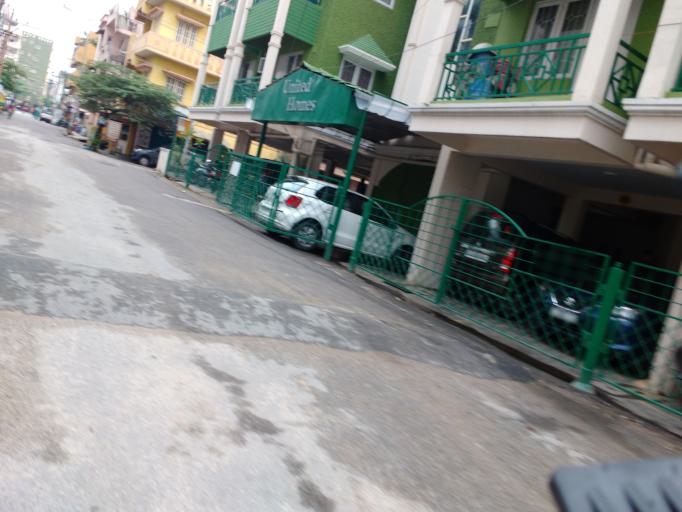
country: IN
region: Karnataka
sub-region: Bangalore Urban
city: Bangalore
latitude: 12.9917
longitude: 77.6676
